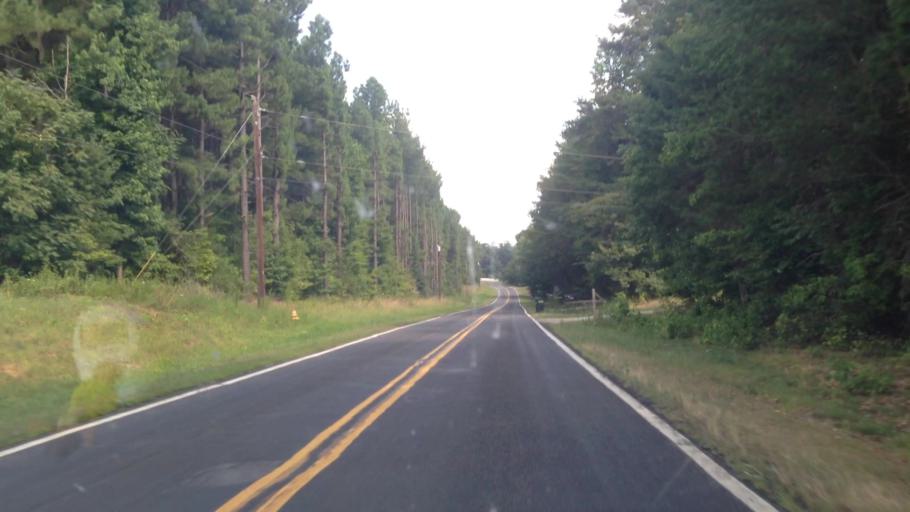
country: US
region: North Carolina
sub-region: Forsyth County
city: Walkertown
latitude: 36.2022
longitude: -80.1050
